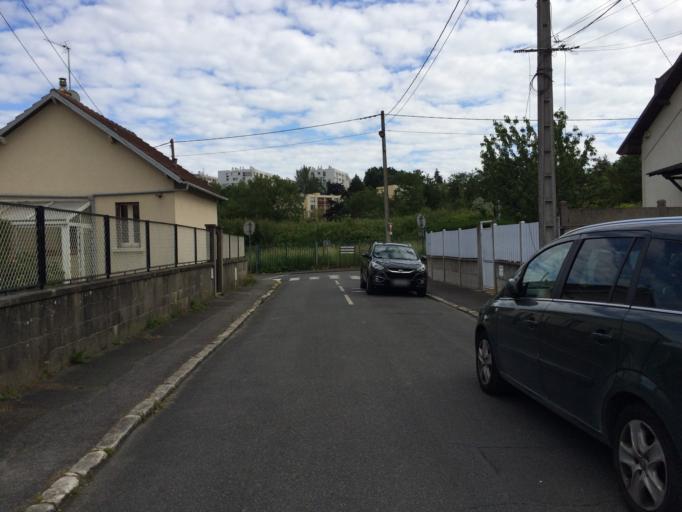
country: FR
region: Ile-de-France
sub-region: Departement de l'Essonne
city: Palaiseau
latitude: 48.7252
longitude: 2.2394
